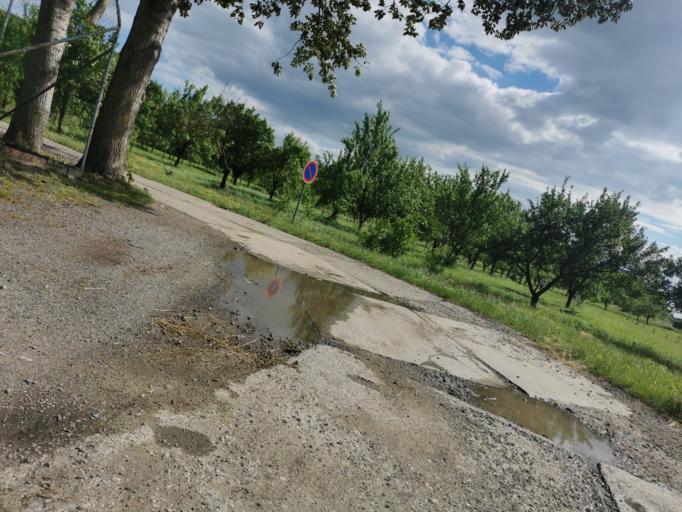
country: CZ
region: South Moravian
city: Vnorovy
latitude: 48.9307
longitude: 17.3444
